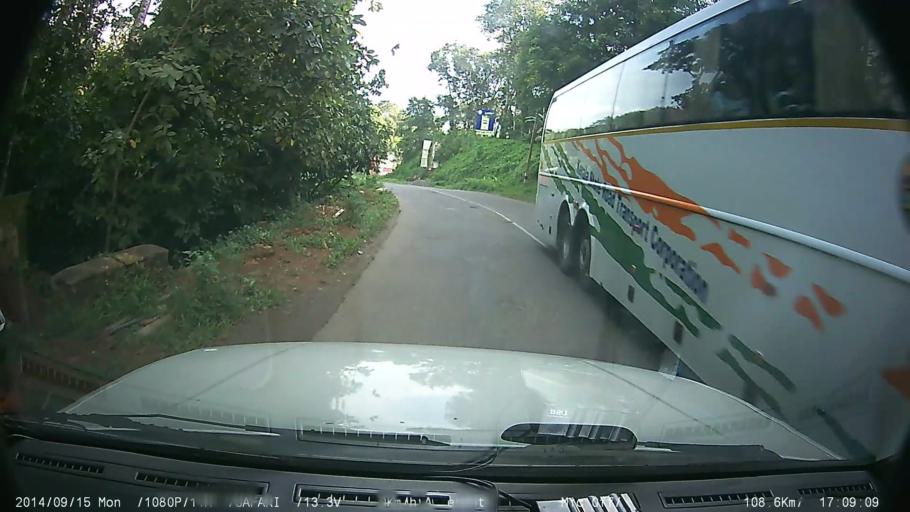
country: IN
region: Kerala
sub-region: Kottayam
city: Palackattumala
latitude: 9.7900
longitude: 76.5791
